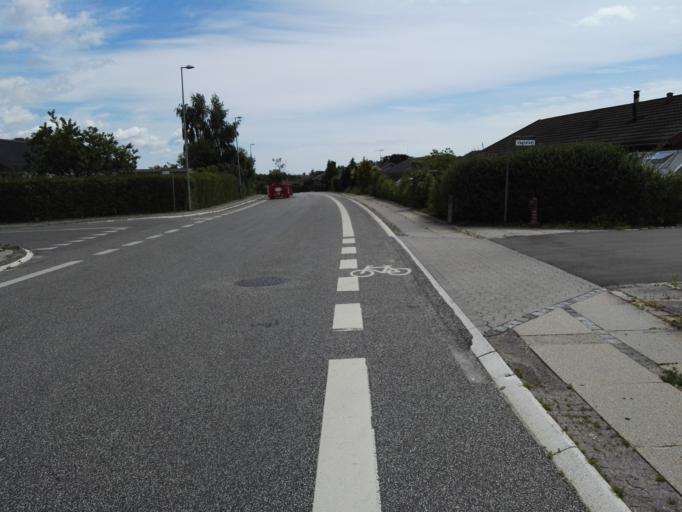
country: DK
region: Capital Region
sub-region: Egedal Kommune
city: Stenlose
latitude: 55.7630
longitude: 12.1877
